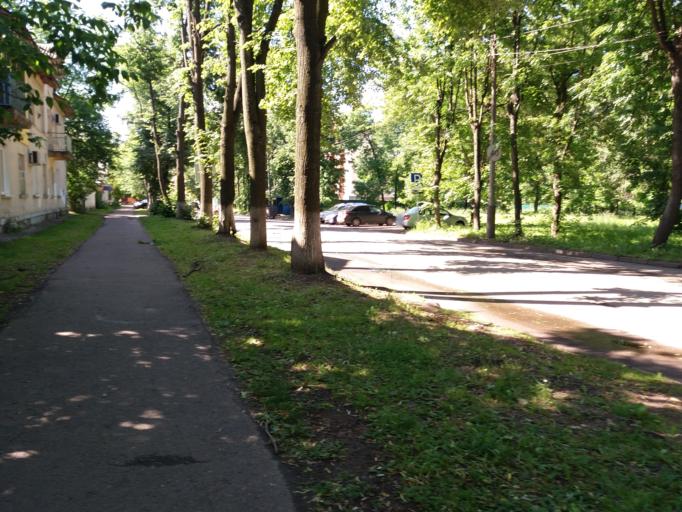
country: RU
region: Jaroslavl
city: Yaroslavl
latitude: 57.6404
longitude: 39.8305
